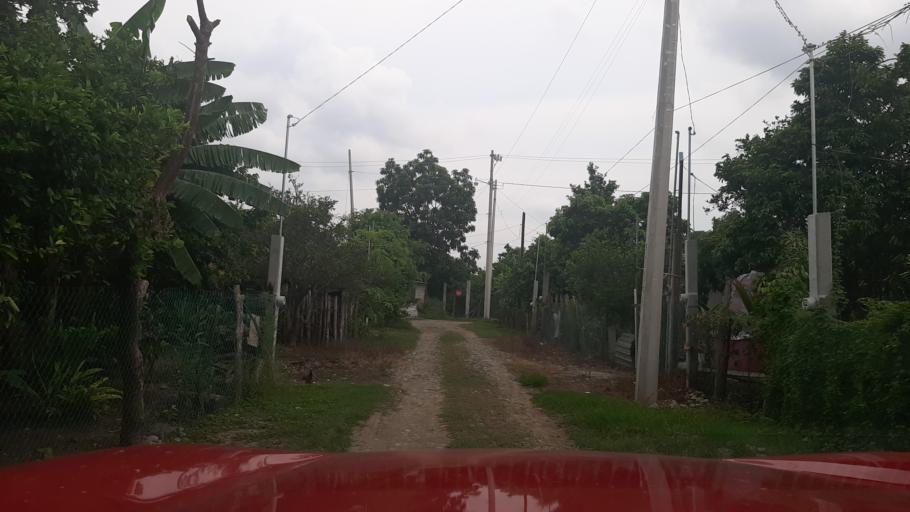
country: MX
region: Veracruz
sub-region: Tihuatlan
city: Ricardo Flores Magon
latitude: 20.5133
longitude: -97.4927
